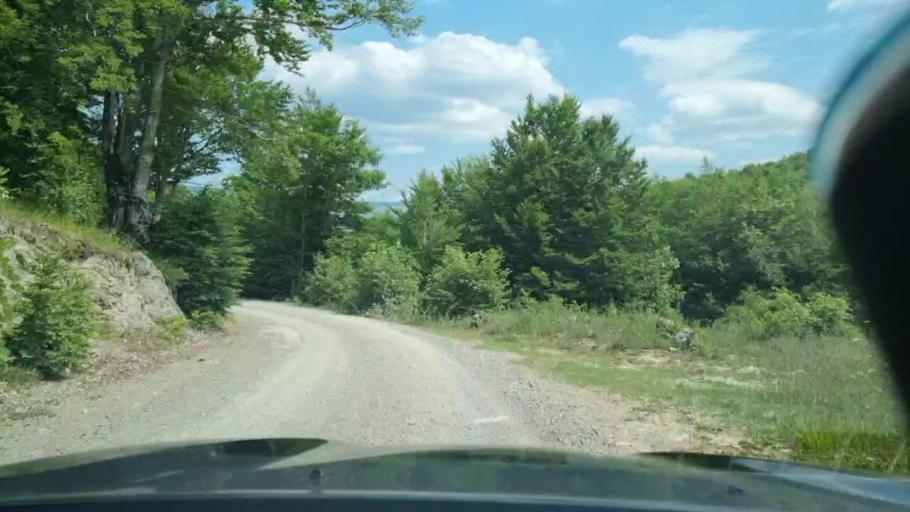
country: BA
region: Federation of Bosnia and Herzegovina
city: Bosansko Grahovo
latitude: 44.2986
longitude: 16.2689
